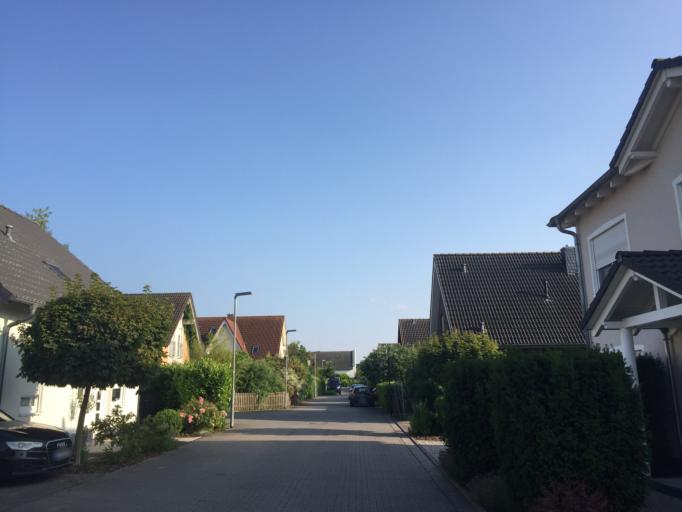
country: DE
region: Hesse
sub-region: Regierungsbezirk Giessen
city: Langgons
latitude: 50.5363
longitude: 8.7274
